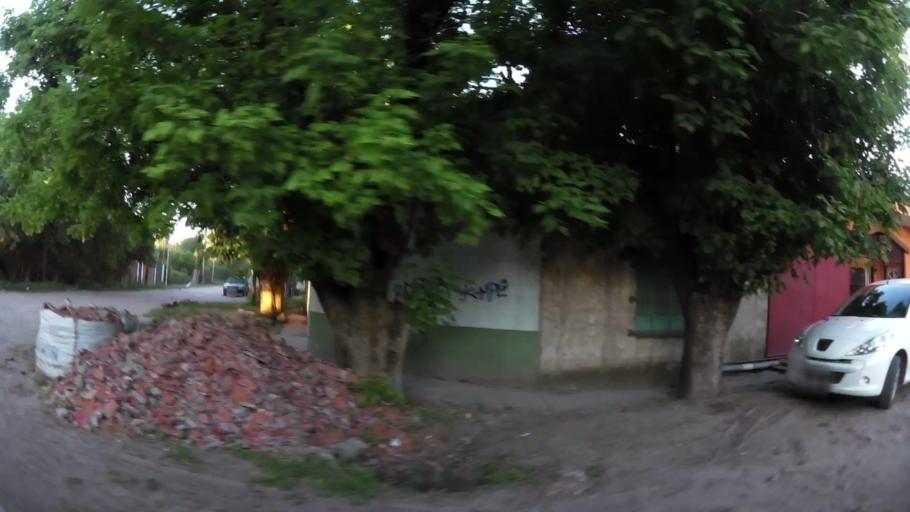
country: AR
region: Buenos Aires
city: Pontevedra
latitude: -34.7940
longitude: -58.6338
